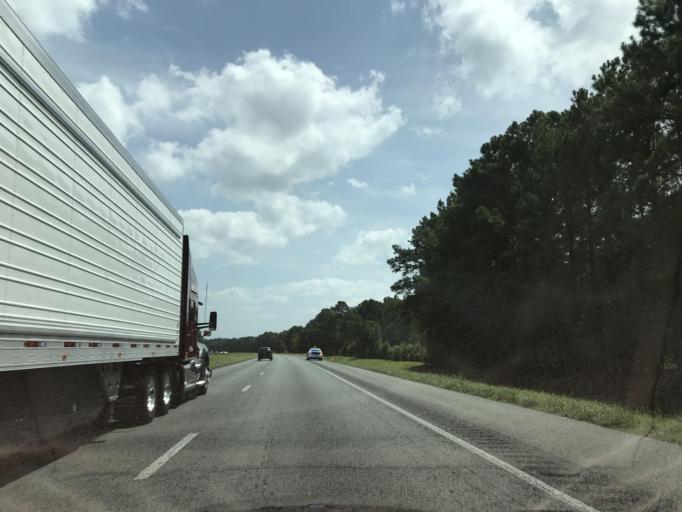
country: US
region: North Carolina
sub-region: Duplin County
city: Warsaw
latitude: 34.9799
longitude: -78.1292
